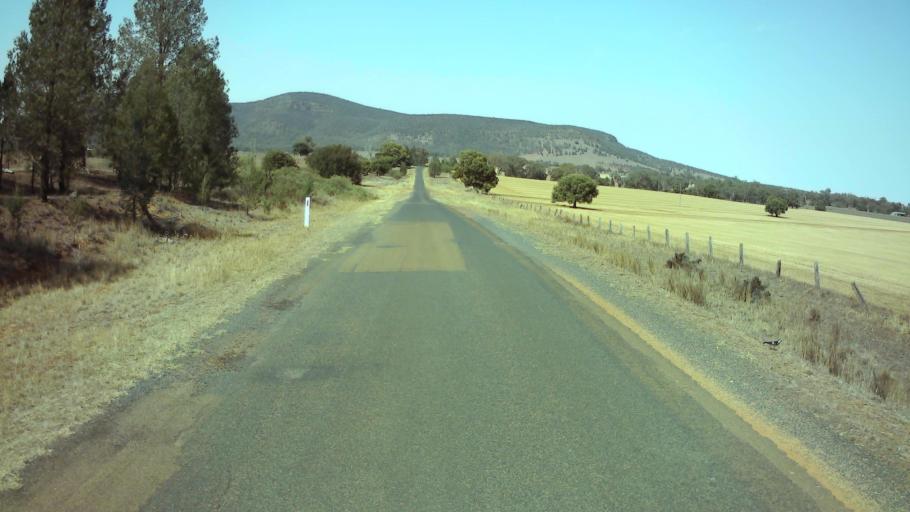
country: AU
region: New South Wales
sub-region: Weddin
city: Grenfell
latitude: -33.8620
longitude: 148.0135
